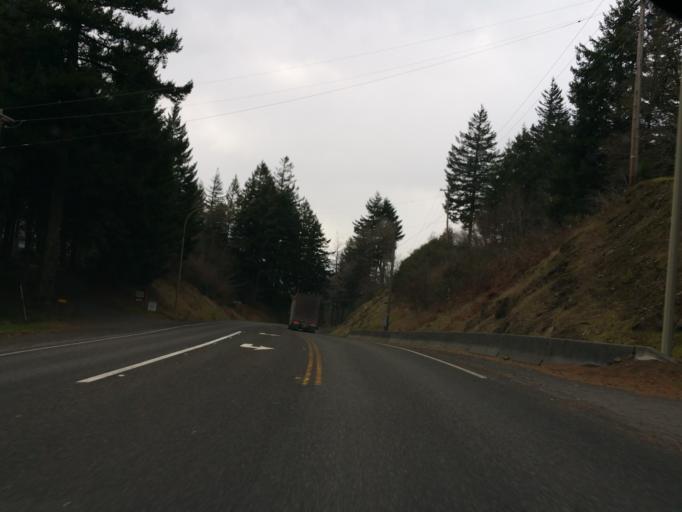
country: US
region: Washington
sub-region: Skamania County
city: Stevenson
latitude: 45.7033
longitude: -121.8579
